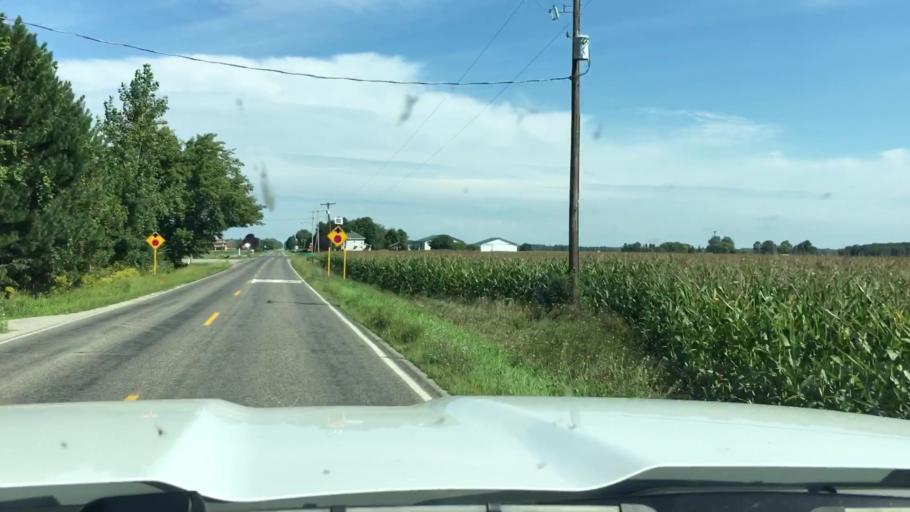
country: US
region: Michigan
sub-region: Midland County
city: Midland
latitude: 43.5231
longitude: -84.2294
